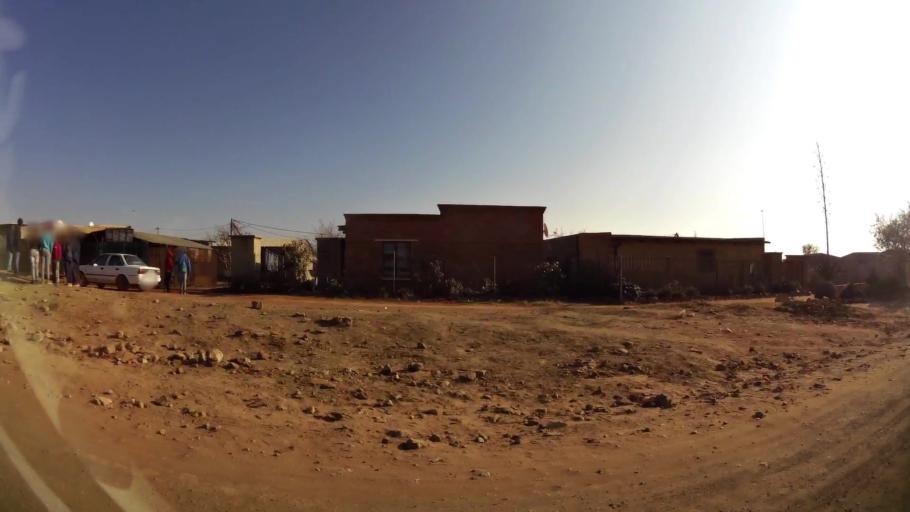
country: ZA
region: Orange Free State
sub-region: Mangaung Metropolitan Municipality
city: Bloemfontein
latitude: -29.2009
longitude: 26.2557
